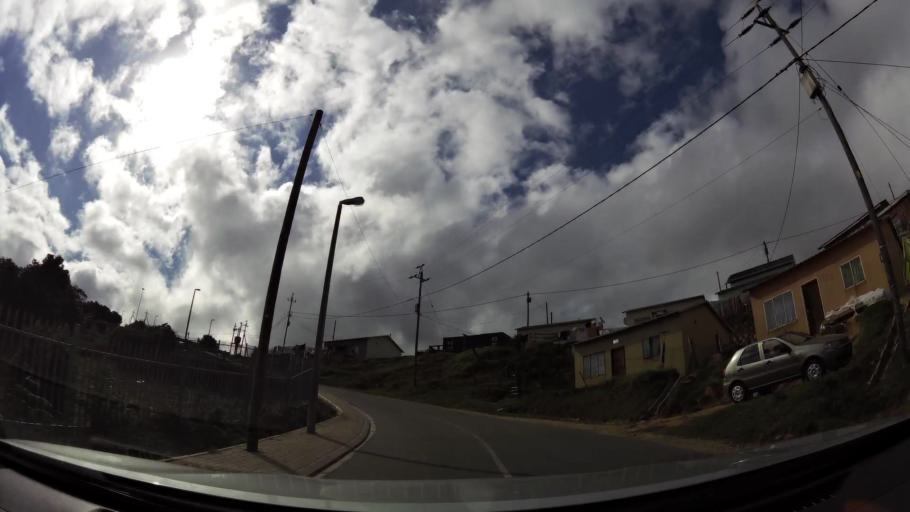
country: ZA
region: Western Cape
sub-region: Eden District Municipality
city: Knysna
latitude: -34.0323
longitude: 23.1000
